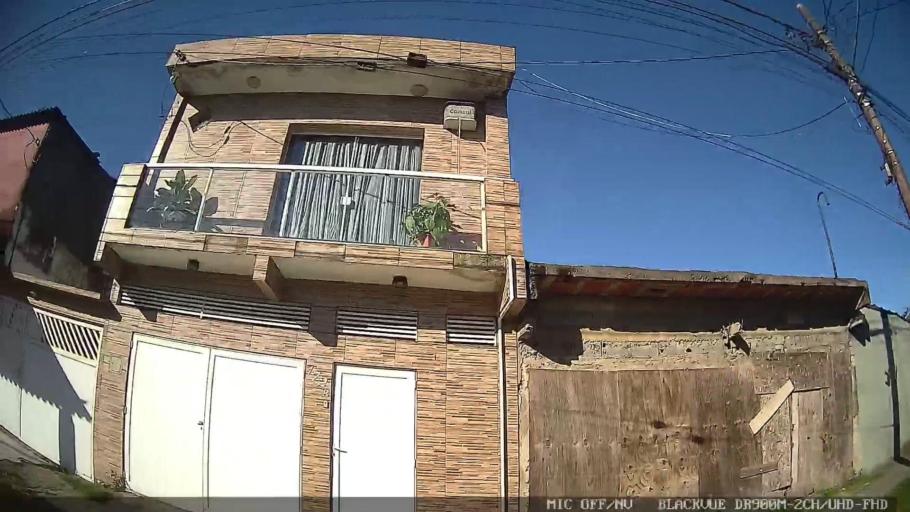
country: BR
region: Sao Paulo
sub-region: Guaruja
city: Guaruja
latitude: -23.9574
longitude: -46.2771
